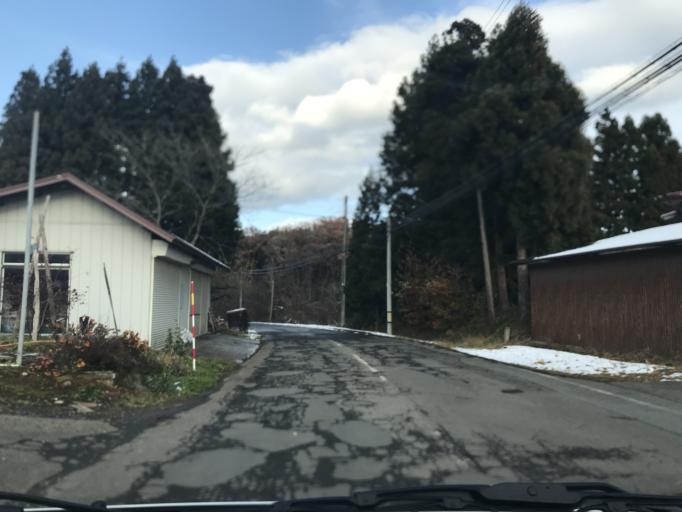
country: JP
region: Iwate
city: Kitakami
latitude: 39.2263
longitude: 141.0464
